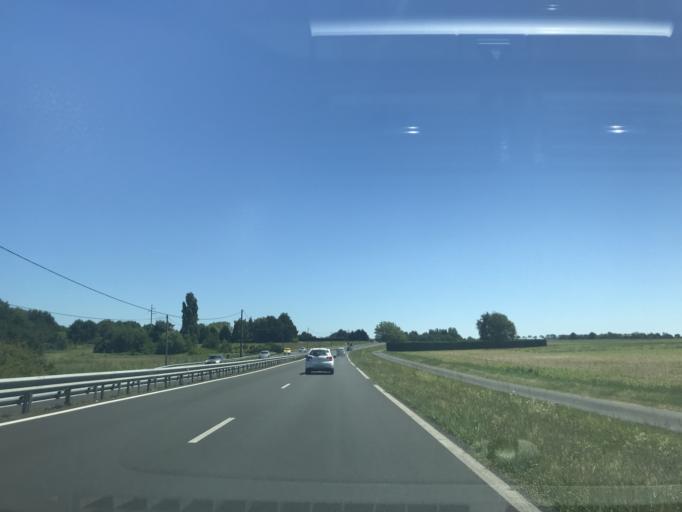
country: FR
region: Poitou-Charentes
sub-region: Departement de la Charente-Maritime
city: Vaux-sur-Mer
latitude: 45.6567
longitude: -1.0561
